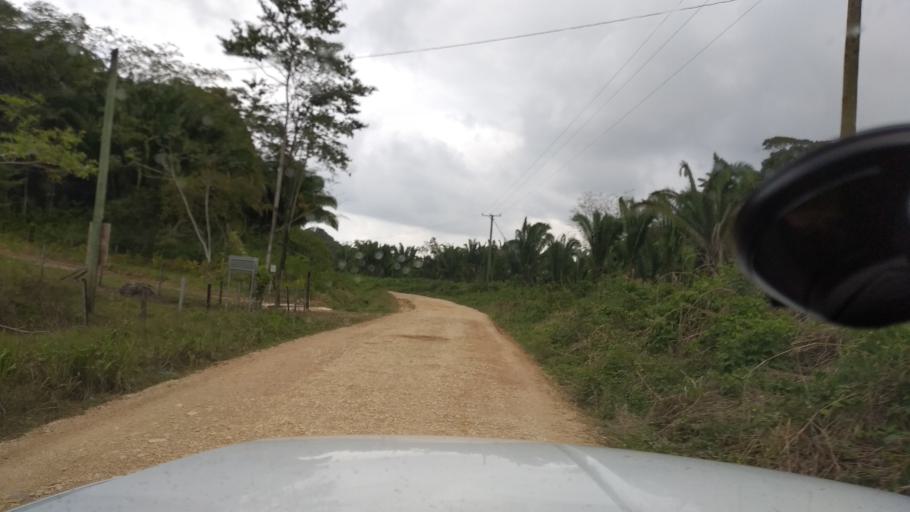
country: BZ
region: Toledo
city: Punta Gorda
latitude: 16.2025
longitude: -89.0352
